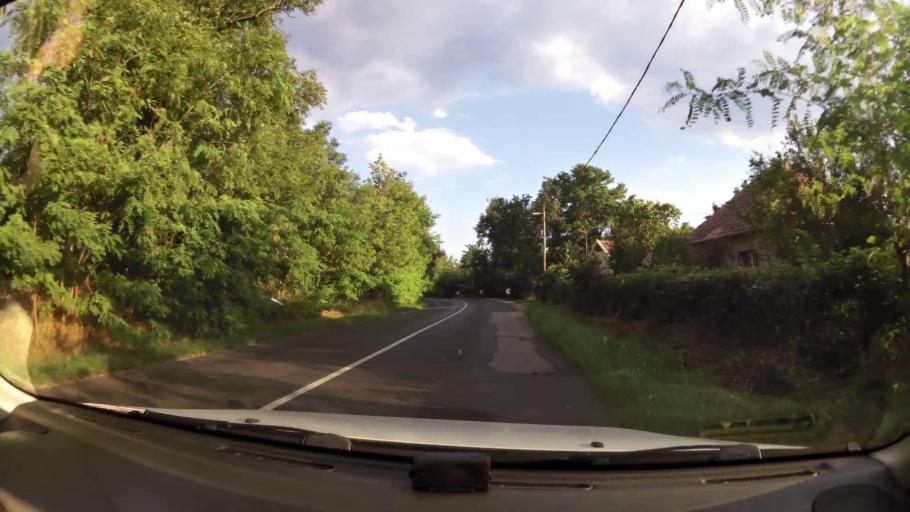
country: HU
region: Pest
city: Tapiosag
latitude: 47.4154
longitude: 19.6092
